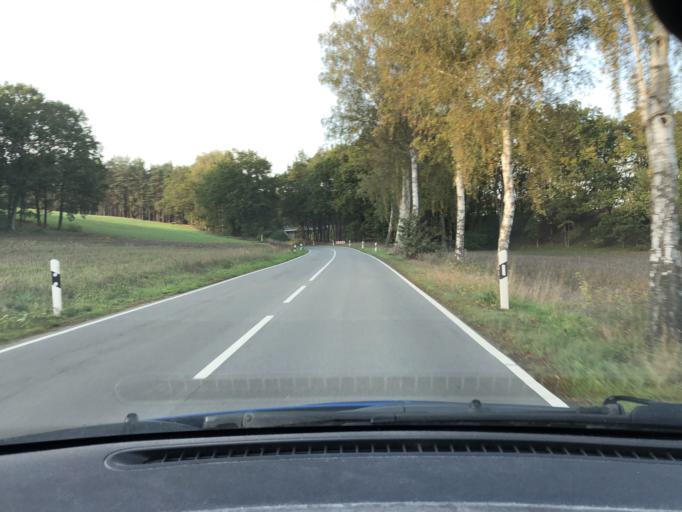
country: DE
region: Lower Saxony
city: Hitzacker
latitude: 53.1315
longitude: 11.0473
